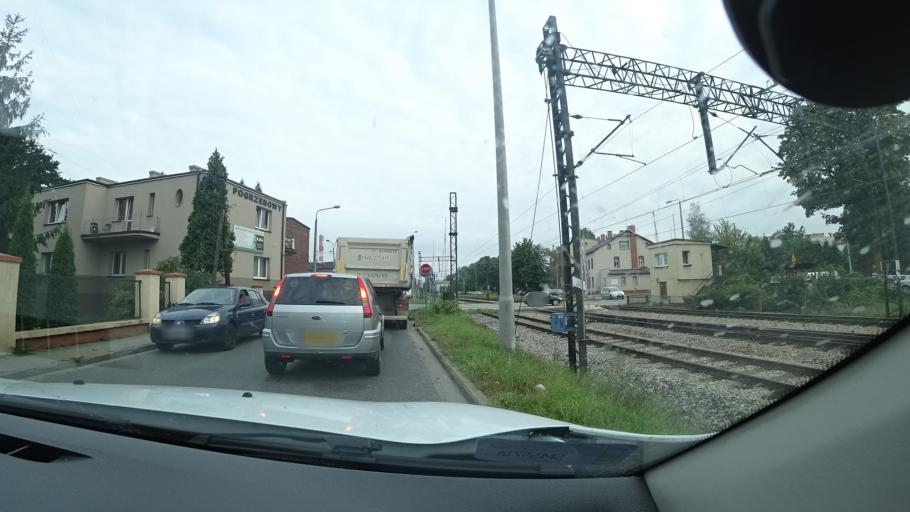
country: PL
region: Silesian Voivodeship
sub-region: Sosnowiec
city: Sosnowiec
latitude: 50.2764
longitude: 19.0658
